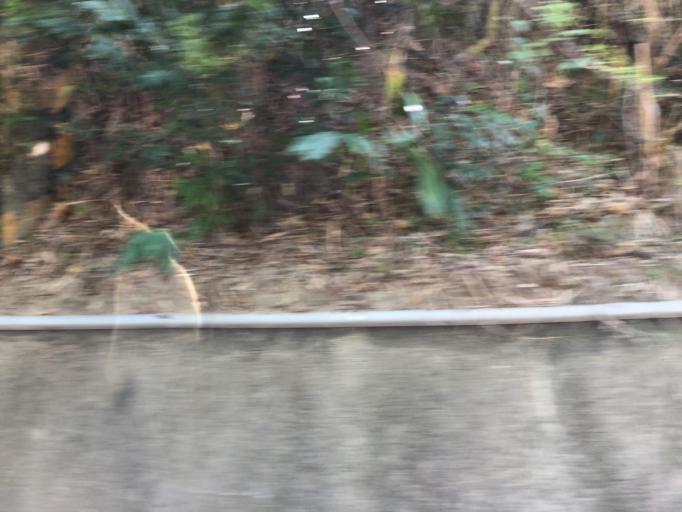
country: TW
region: Taiwan
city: Yujing
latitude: 23.0574
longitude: 120.3788
